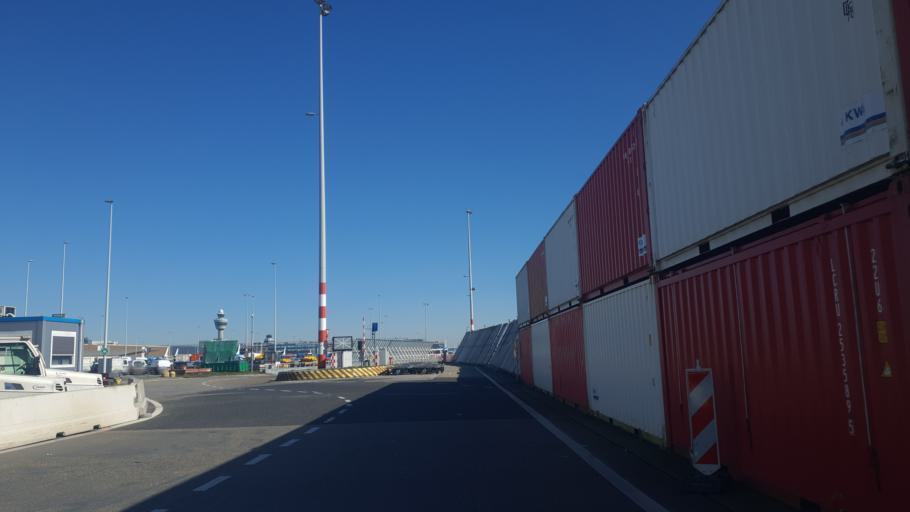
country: NL
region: North Holland
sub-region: Gemeente Aalsmeer
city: Aalsmeer
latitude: 52.2973
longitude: 4.7487
